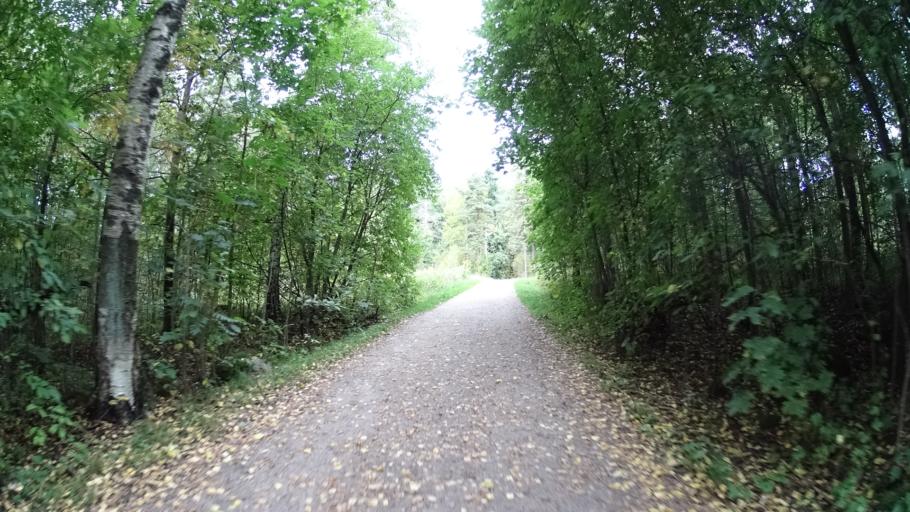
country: FI
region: Uusimaa
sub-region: Helsinki
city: Teekkarikylae
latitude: 60.2166
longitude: 24.8526
